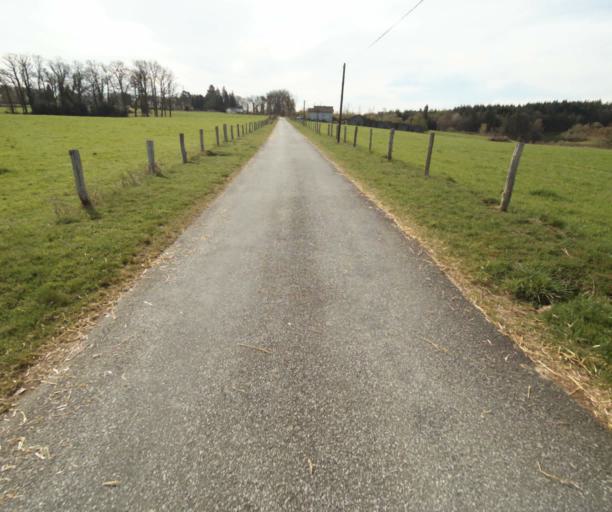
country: FR
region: Limousin
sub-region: Departement de la Correze
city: Correze
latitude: 45.3354
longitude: 1.8678
